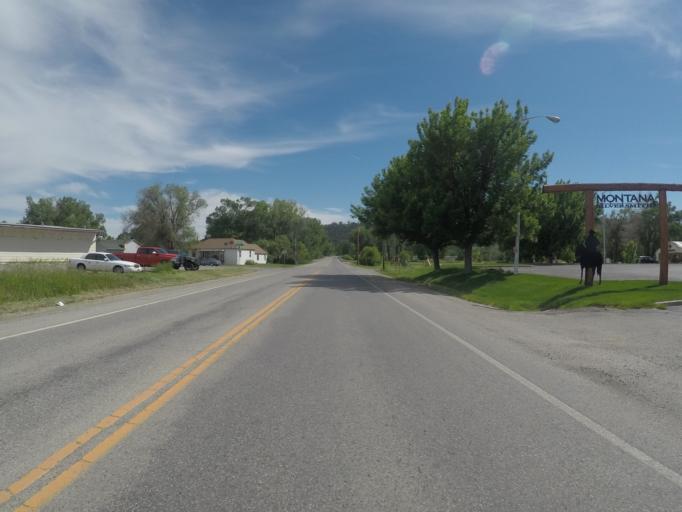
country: US
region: Montana
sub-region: Stillwater County
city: Columbus
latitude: 45.6337
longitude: -109.2534
